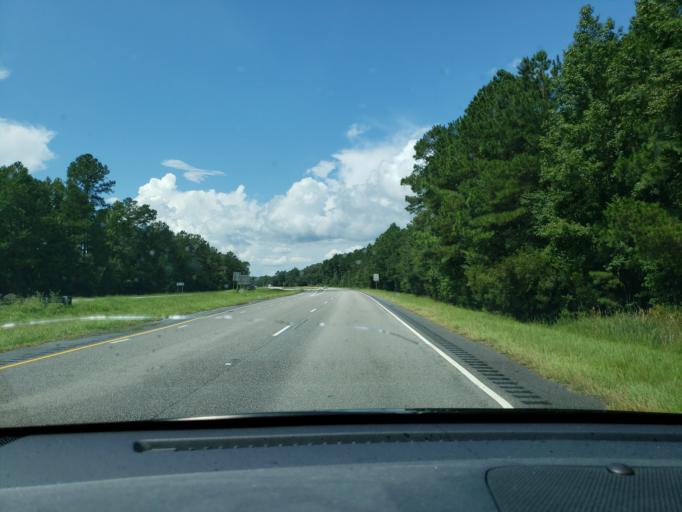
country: US
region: North Carolina
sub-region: Bladen County
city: Elizabethtown
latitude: 34.6425
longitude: -78.6767
